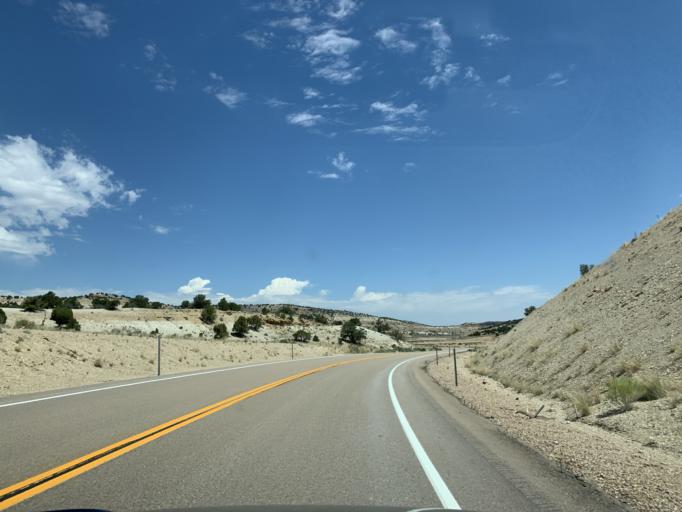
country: US
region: Utah
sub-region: Duchesne County
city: Duchesne
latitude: 39.9569
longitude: -110.1903
